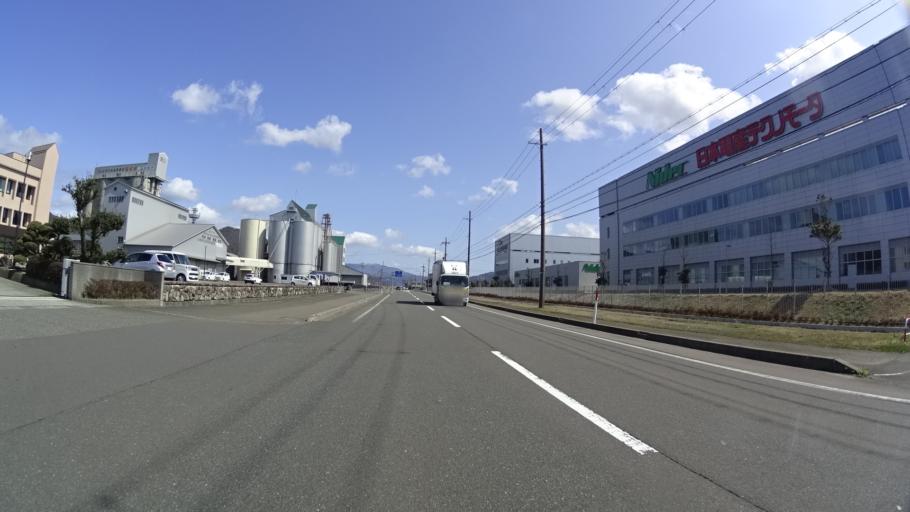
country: JP
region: Fukui
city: Obama
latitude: 35.4889
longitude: 135.7774
